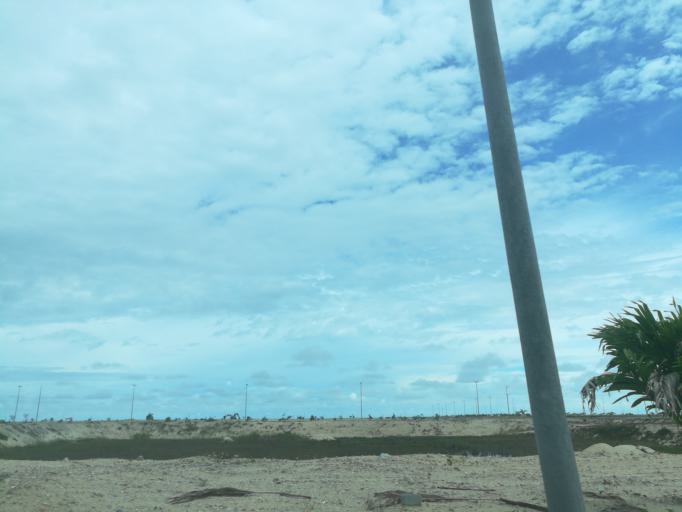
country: NG
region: Lagos
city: Ikoyi
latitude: 6.4119
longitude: 3.4198
